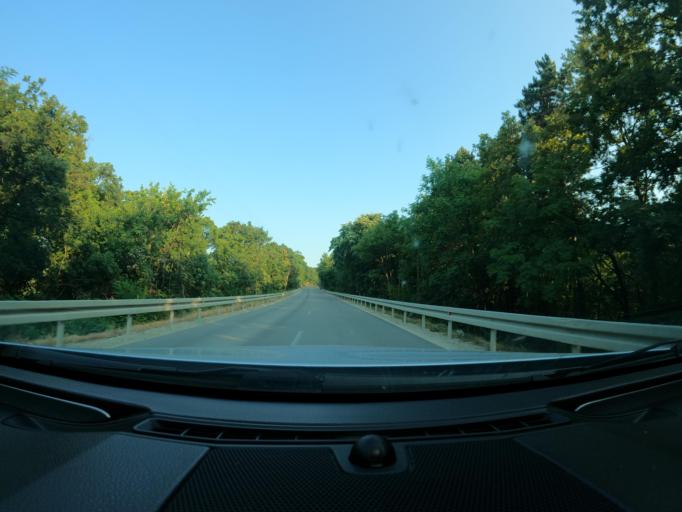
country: RS
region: Autonomna Pokrajina Vojvodina
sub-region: Juznobacki Okrug
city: Beocin
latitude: 45.1651
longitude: 19.7137
